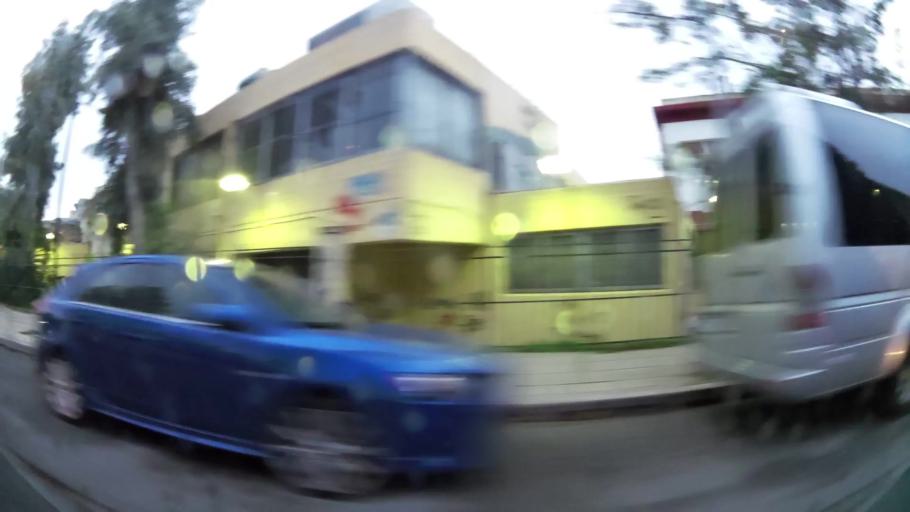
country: GR
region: Attica
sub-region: Nomarchia Athinas
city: Dhafni
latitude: 37.9515
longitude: 23.7400
